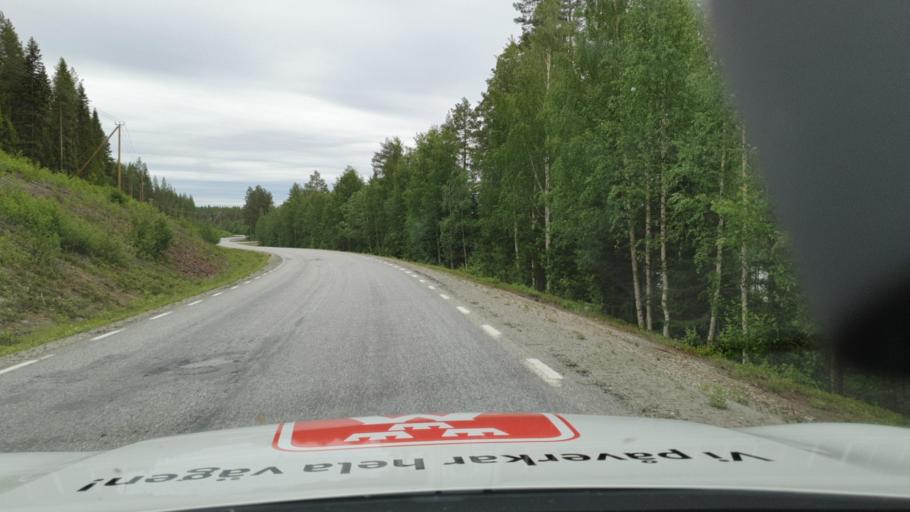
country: SE
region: Vaesterbotten
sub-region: Lycksele Kommun
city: Lycksele
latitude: 64.0980
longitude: 18.3671
